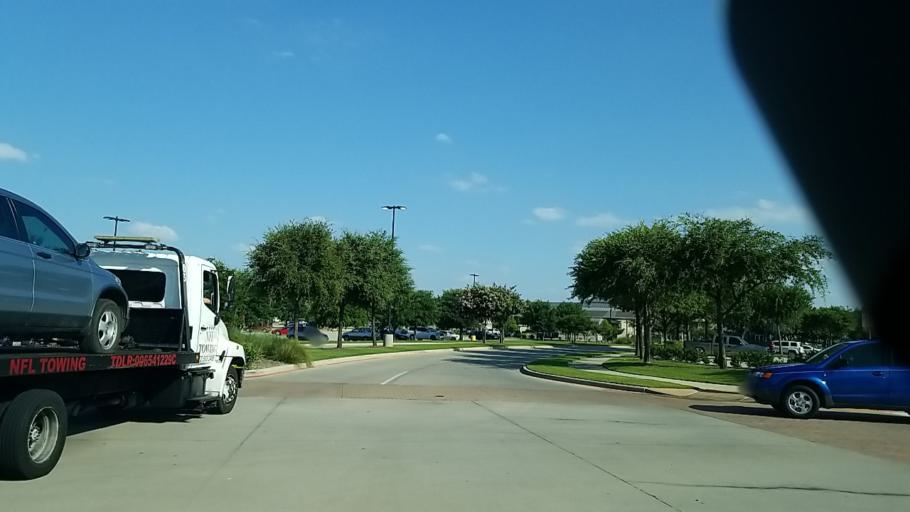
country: US
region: Texas
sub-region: Denton County
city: Copper Canyon
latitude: 33.0760
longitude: -97.0798
